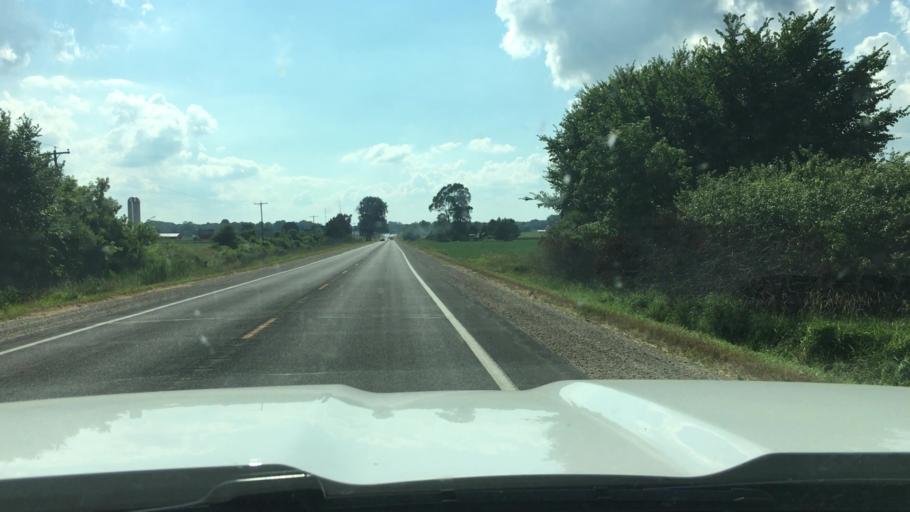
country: US
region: Michigan
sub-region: Montcalm County
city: Stanton
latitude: 43.1782
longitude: -85.0583
